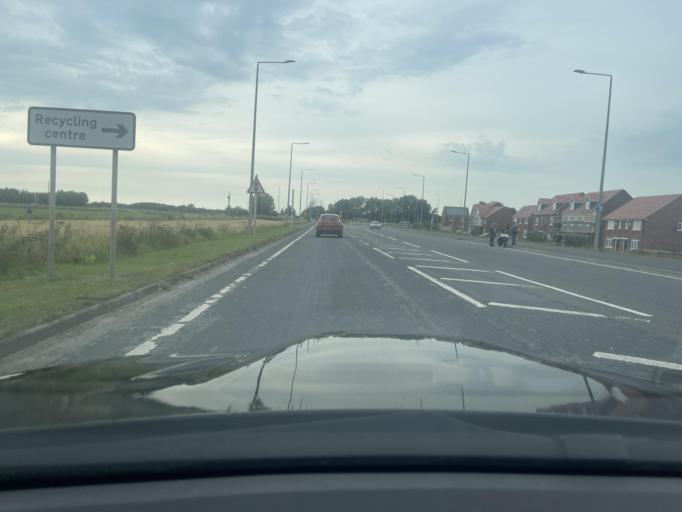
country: GB
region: England
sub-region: Lancashire
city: Leyland
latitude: 53.7113
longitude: -2.7161
